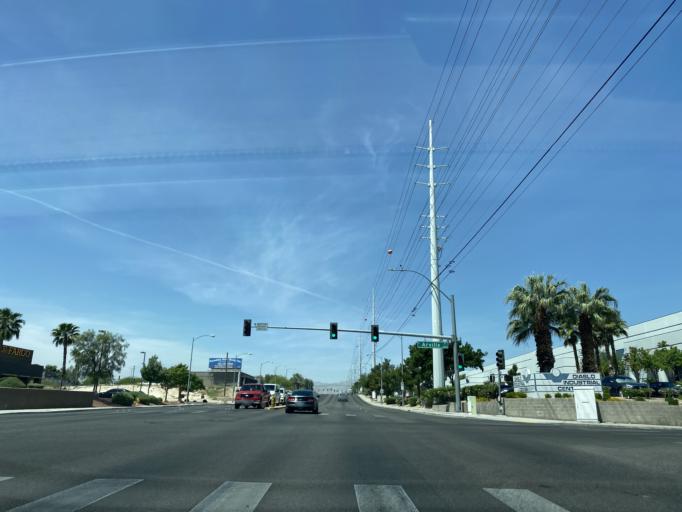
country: US
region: Nevada
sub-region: Clark County
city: Spring Valley
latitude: 36.0864
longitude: -115.1988
